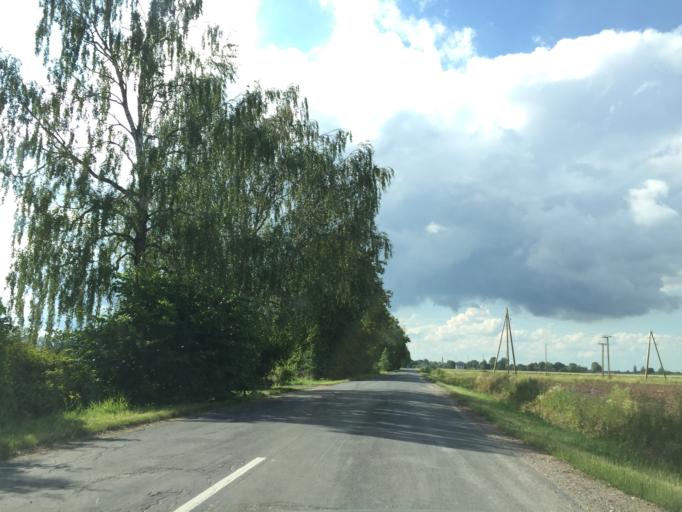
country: LV
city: Tervete
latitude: 56.5590
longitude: 23.3915
